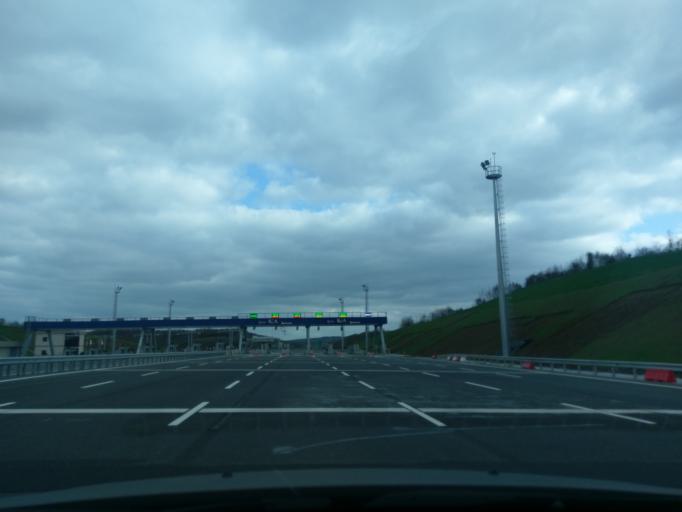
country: TR
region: Istanbul
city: Kemerburgaz
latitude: 41.2378
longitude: 28.8195
